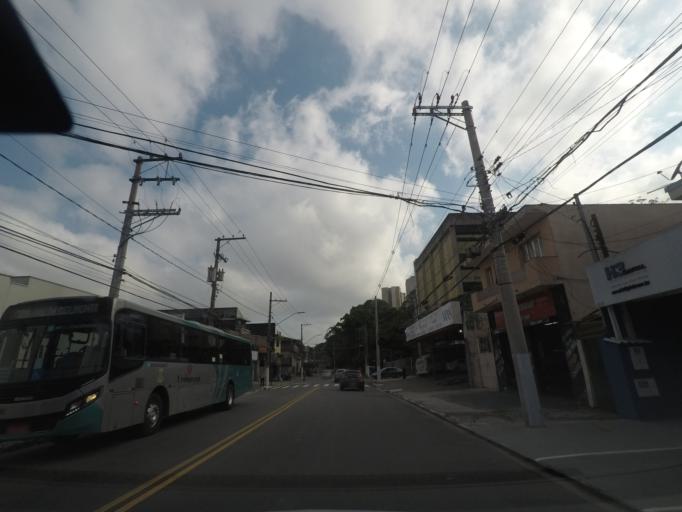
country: BR
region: Sao Paulo
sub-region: Osasco
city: Osasco
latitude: -23.5574
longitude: -46.7811
